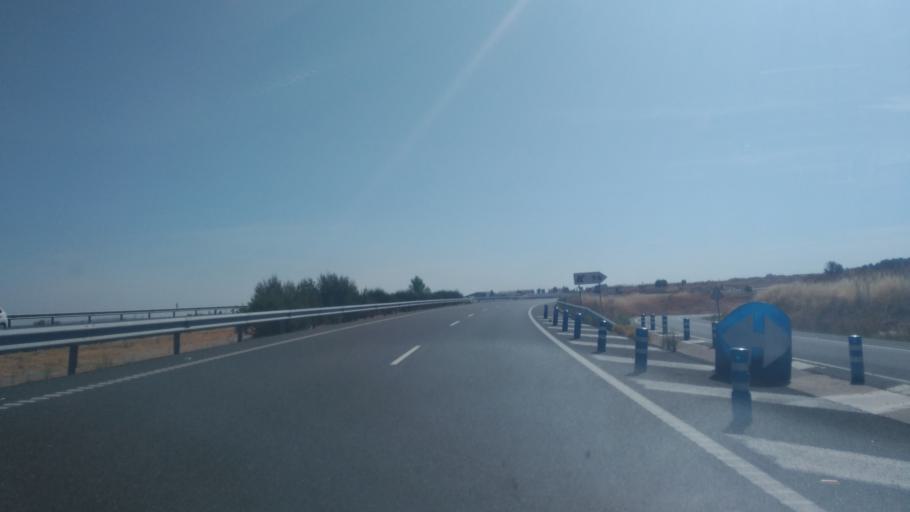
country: ES
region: Castille and Leon
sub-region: Provincia de Salamanca
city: Santa Marta de Tormes
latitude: 40.9447
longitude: -5.6036
